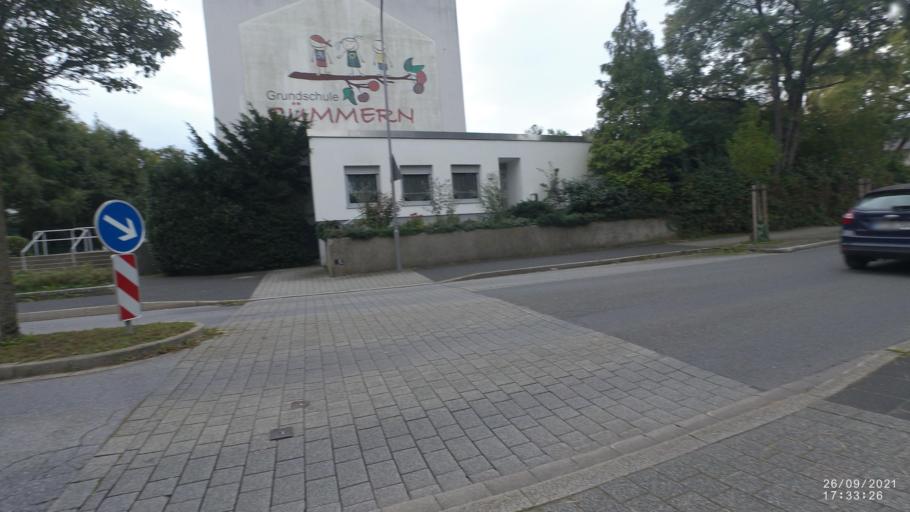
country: DE
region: North Rhine-Westphalia
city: Iserlohn
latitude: 51.4196
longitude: 7.7141
